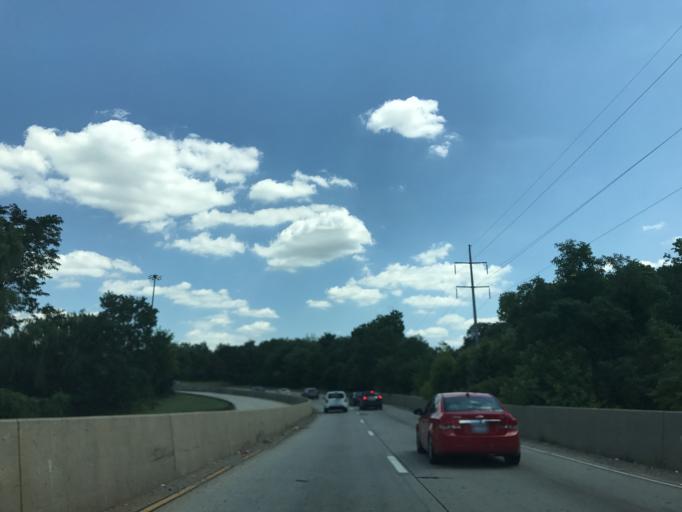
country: US
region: Maryland
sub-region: Prince George's County
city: Colmar Manor
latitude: 38.9177
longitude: -76.9534
